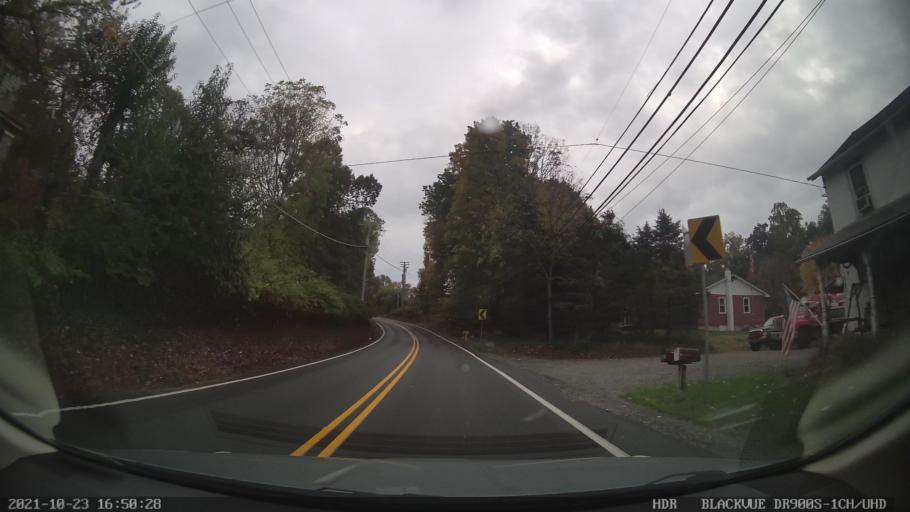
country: US
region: Pennsylvania
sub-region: Berks County
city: Red Lion
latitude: 40.4779
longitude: -75.6147
